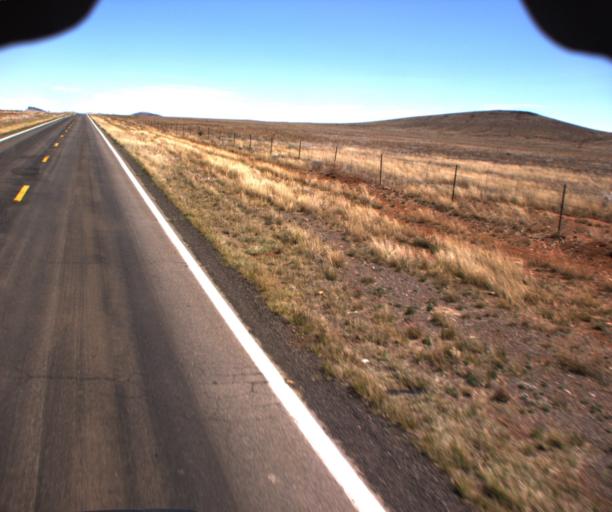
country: US
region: Arizona
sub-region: Cochise County
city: Douglas
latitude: 31.5835
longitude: -109.2508
